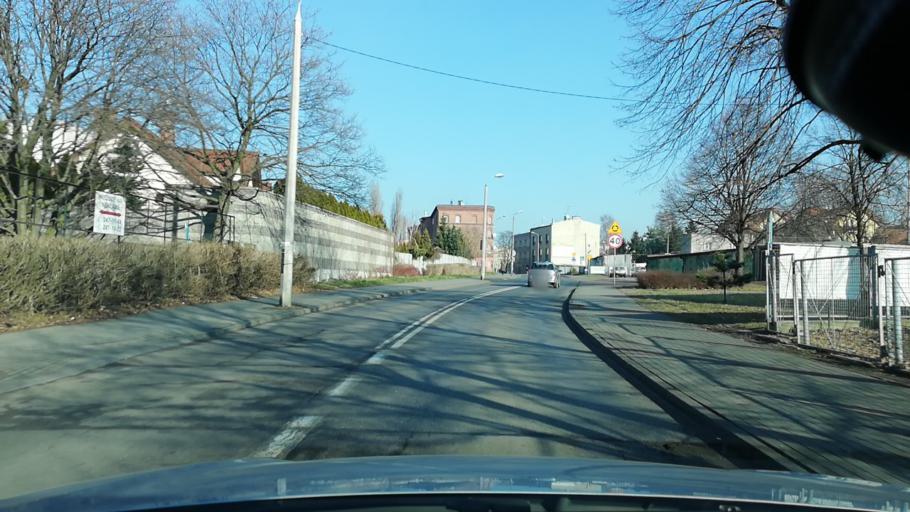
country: PL
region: Silesian Voivodeship
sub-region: Swietochlowice
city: Swietochlowice
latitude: 50.2697
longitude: 18.9310
